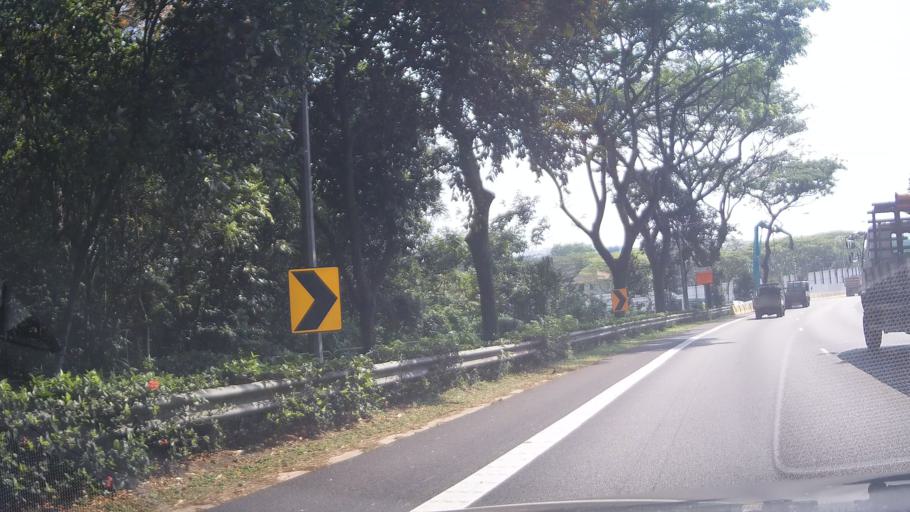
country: MY
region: Johor
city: Johor Bahru
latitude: 1.3393
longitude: 103.6785
